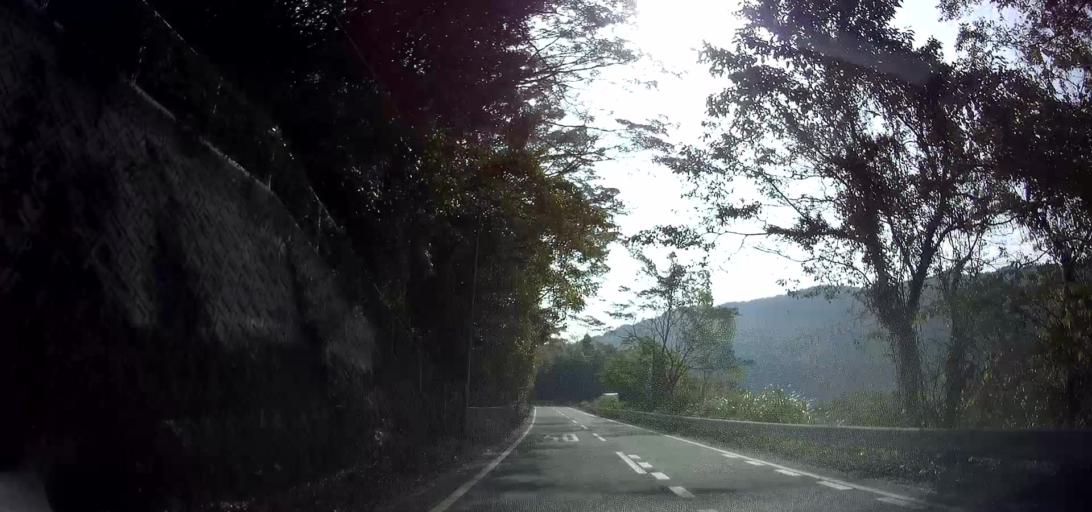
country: JP
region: Nagasaki
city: Shimabara
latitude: 32.6768
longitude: 130.2065
